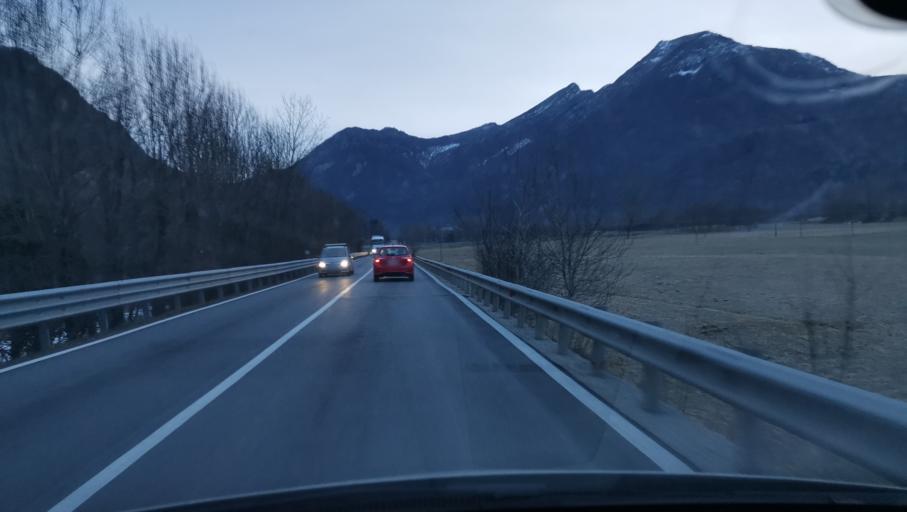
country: IT
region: Piedmont
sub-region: Provincia di Cuneo
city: Valloriate
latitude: 44.3134
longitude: 7.3408
